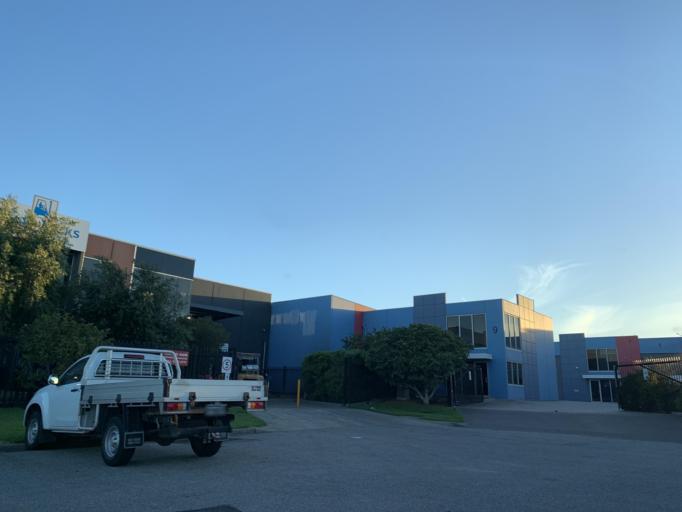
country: AU
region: Victoria
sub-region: Kingston
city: Aspendale Gardens
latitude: -38.0090
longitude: 145.1066
